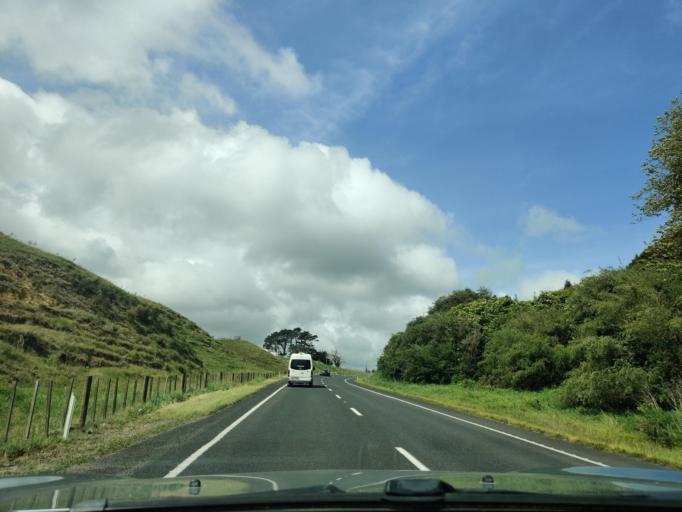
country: NZ
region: Manawatu-Wanganui
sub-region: Wanganui District
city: Wanganui
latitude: -39.8235
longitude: 174.8436
